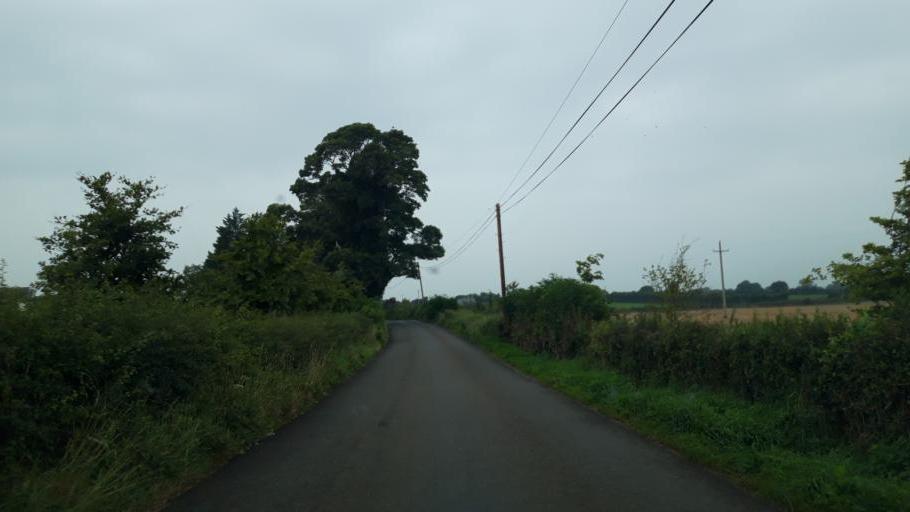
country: IE
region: Leinster
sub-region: Kilkenny
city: Thomastown
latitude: 52.6217
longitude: -7.0867
